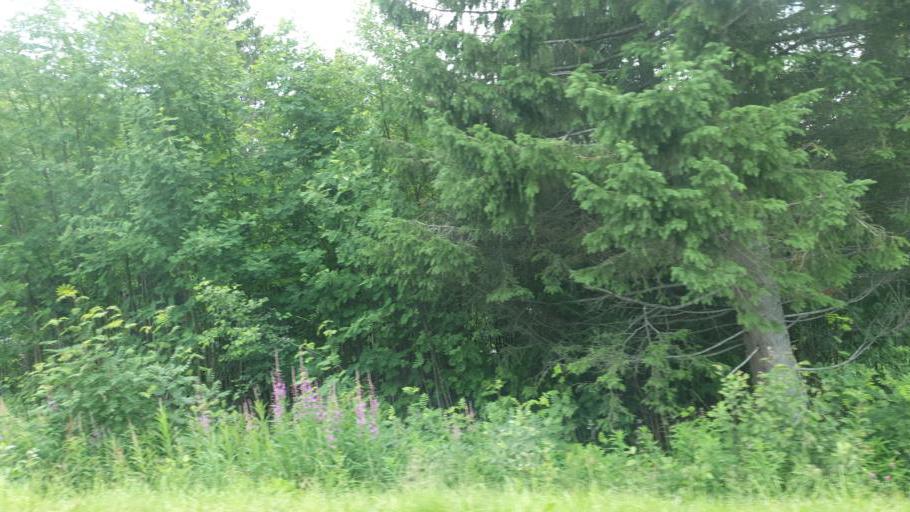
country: NO
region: Sor-Trondelag
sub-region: Rennebu
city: Berkak
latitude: 62.8333
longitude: 10.0051
